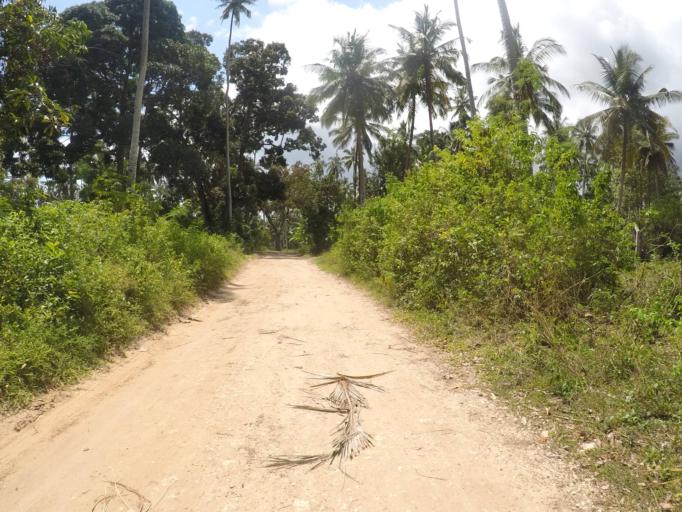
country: TZ
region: Zanzibar North
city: Mkokotoni
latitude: -5.9916
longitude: 39.1868
